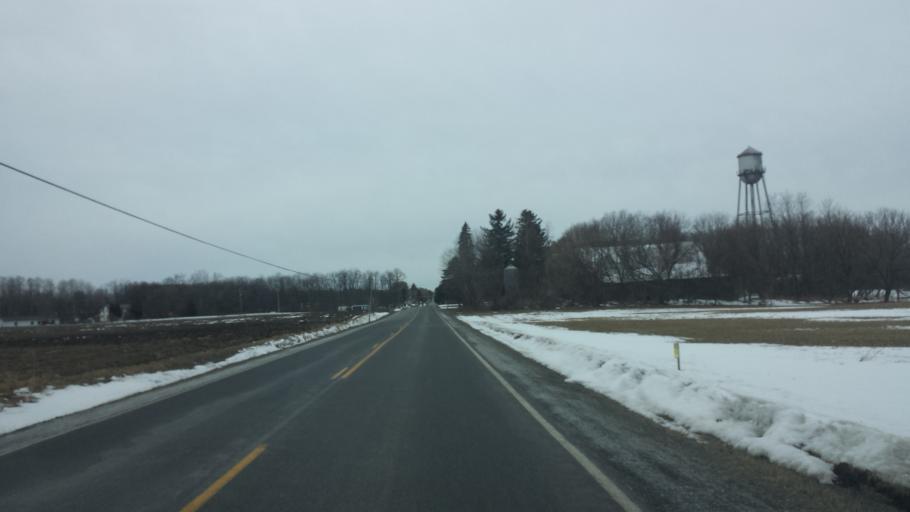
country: US
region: New York
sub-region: Tompkins County
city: Northwest Ithaca
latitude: 42.4961
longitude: -76.5899
